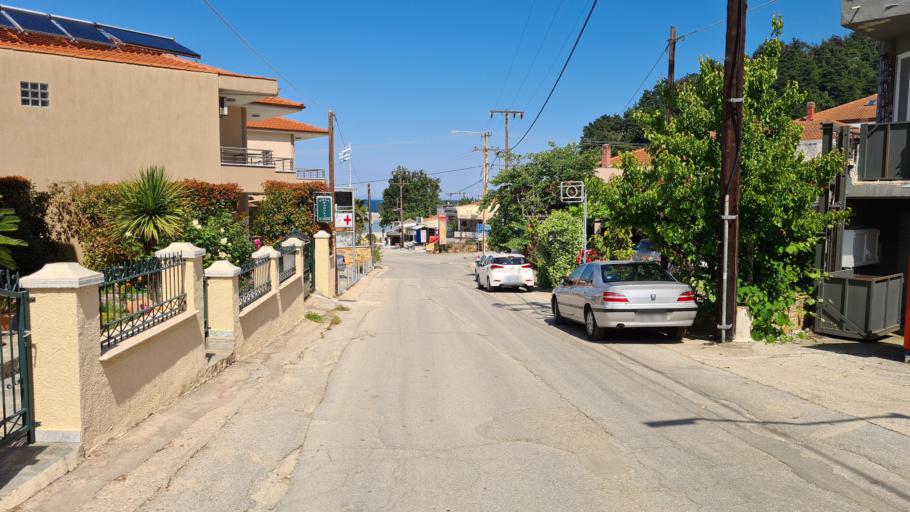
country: GR
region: East Macedonia and Thrace
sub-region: Nomos Kavalas
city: Potamia
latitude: 40.7084
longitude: 24.7579
